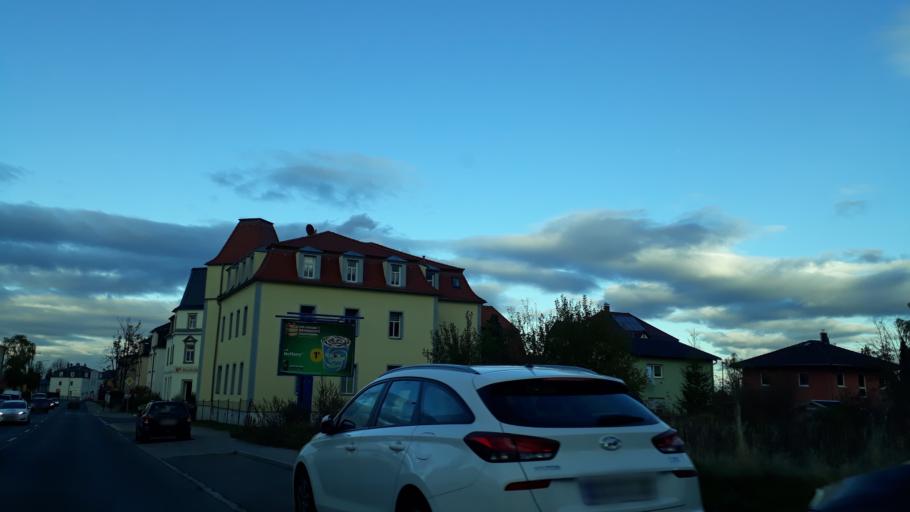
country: DE
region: Saxony
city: Bannewitz
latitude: 51.0049
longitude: 13.6880
